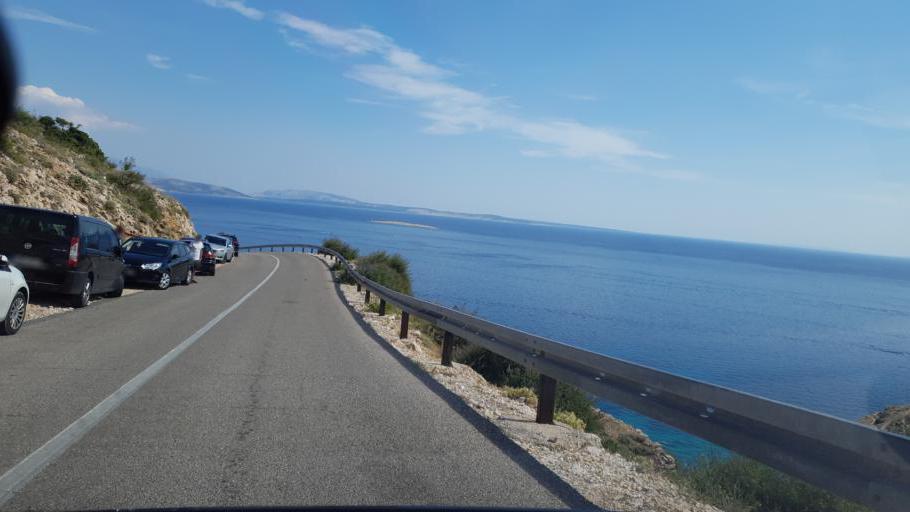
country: HR
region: Primorsko-Goranska
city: Punat
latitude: 44.9692
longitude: 14.6630
